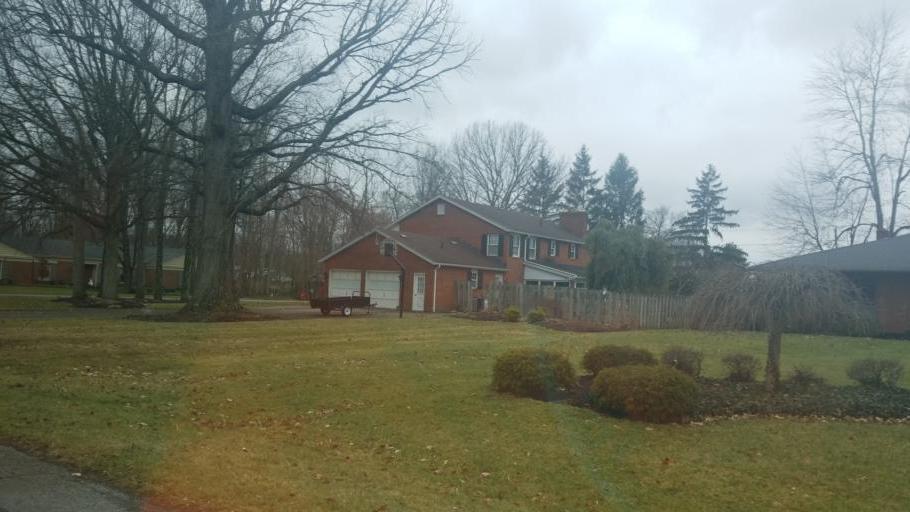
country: US
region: Ohio
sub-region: Crawford County
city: Galion
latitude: 40.7470
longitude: -82.8095
